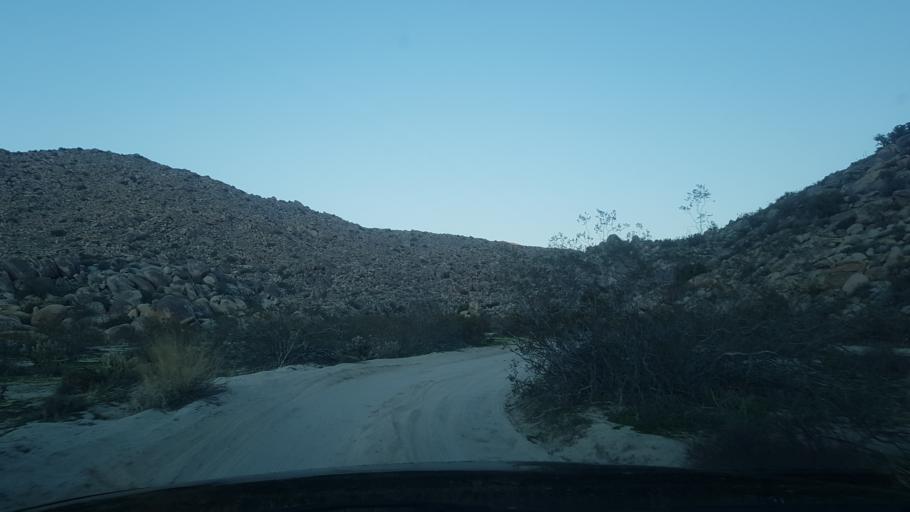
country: US
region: California
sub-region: San Diego County
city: Borrego Springs
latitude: 33.0187
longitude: -116.3618
